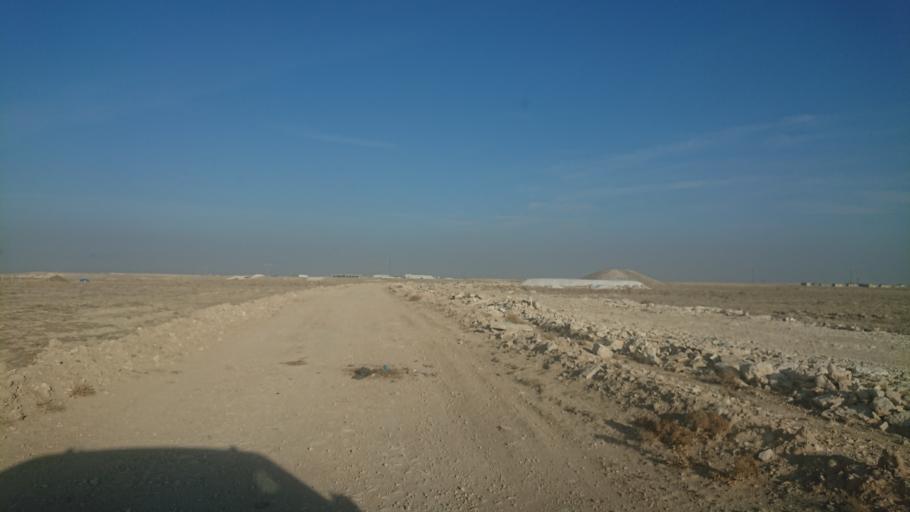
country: TR
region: Aksaray
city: Sultanhani
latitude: 38.1437
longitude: 33.5768
